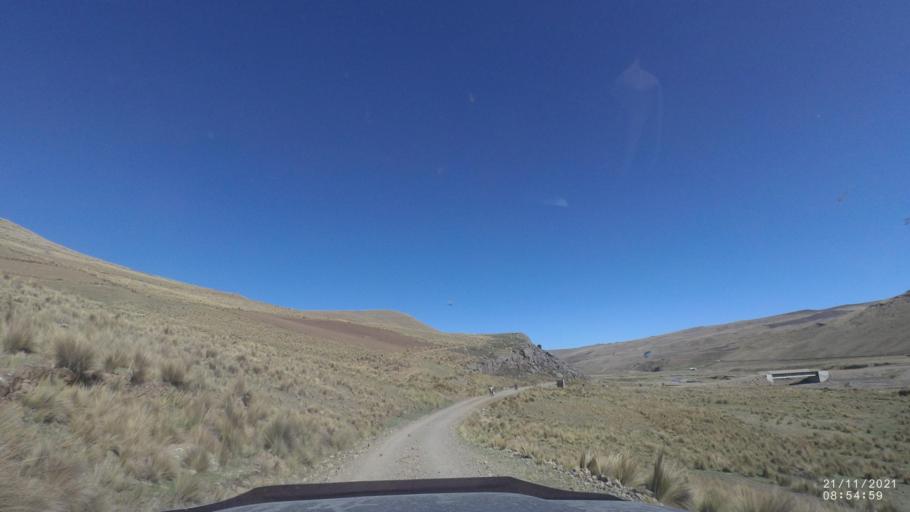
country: BO
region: Cochabamba
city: Cochabamba
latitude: -17.2006
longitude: -66.2463
